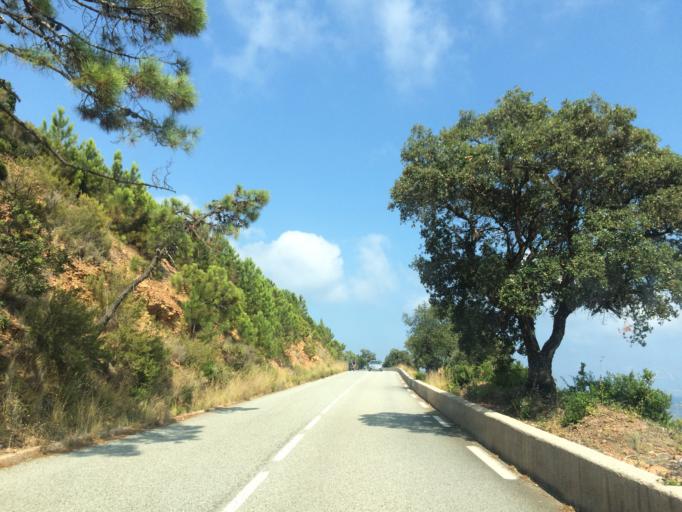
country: FR
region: Provence-Alpes-Cote d'Azur
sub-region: Departement des Alpes-Maritimes
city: Theoule-sur-Mer
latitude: 43.4478
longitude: 6.9101
